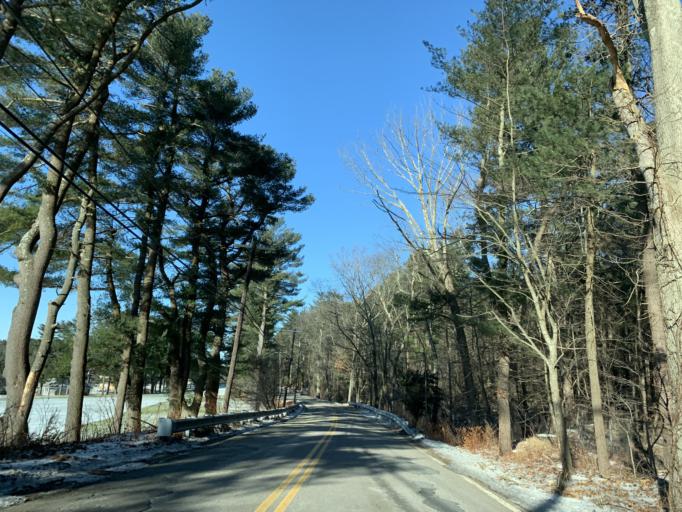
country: US
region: Massachusetts
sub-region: Norfolk County
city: Canton
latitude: 42.1988
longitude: -71.1266
